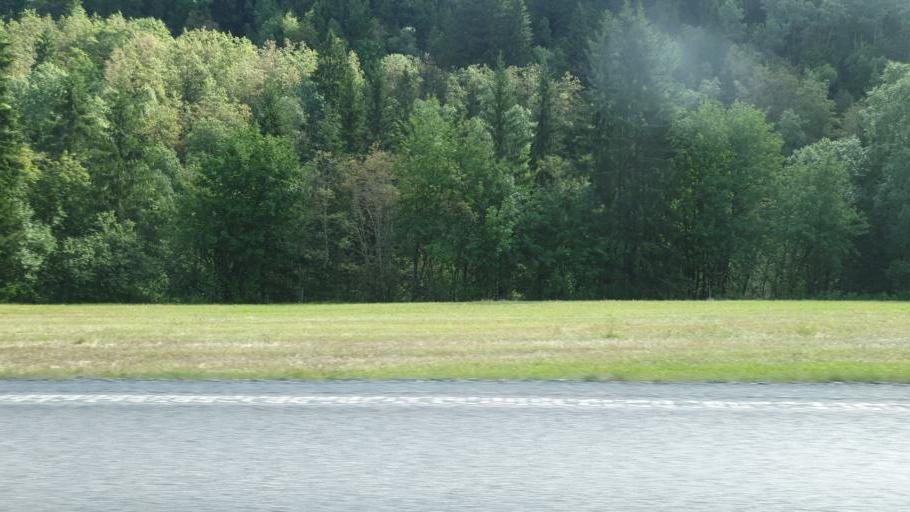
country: NO
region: Sor-Trondelag
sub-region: Midtre Gauldal
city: Storen
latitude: 62.9856
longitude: 10.2437
